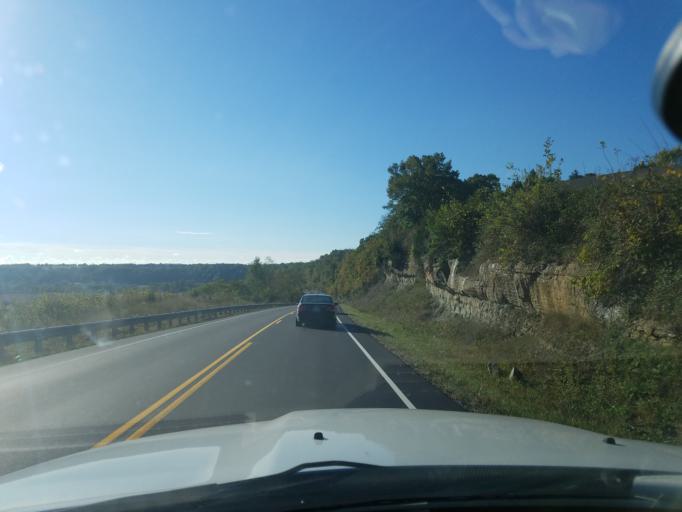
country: US
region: Kentucky
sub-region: Nelson County
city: Bardstown
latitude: 37.7724
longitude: -85.3583
